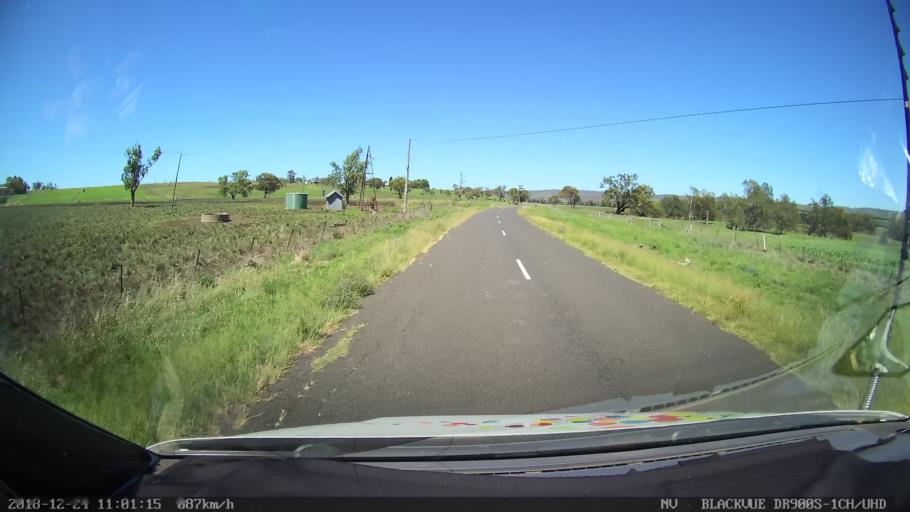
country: AU
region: New South Wales
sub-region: Upper Hunter Shire
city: Merriwa
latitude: -32.0753
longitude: 150.3864
